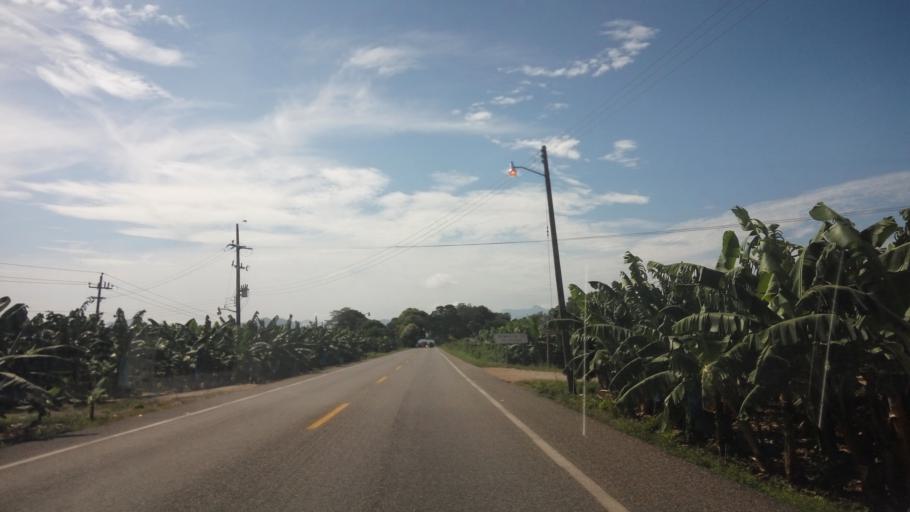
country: MX
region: Tabasco
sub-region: Teapa
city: Eureka y Belen
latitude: 17.6310
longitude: -92.9649
